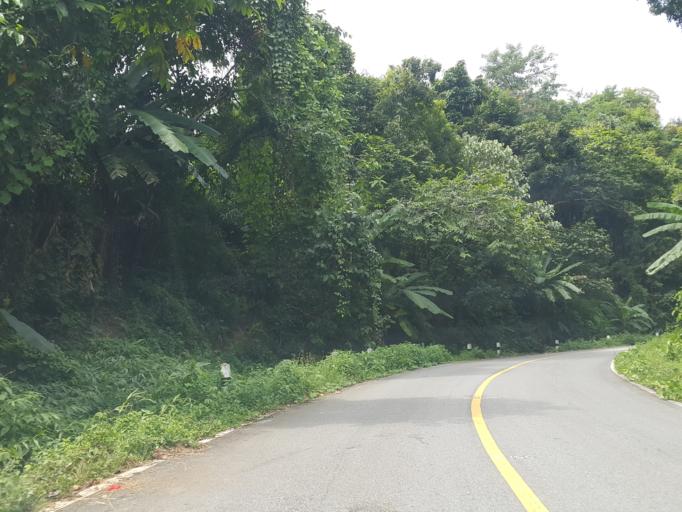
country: TH
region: Mae Hong Son
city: Mae Hong Son
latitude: 19.4846
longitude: 97.9598
